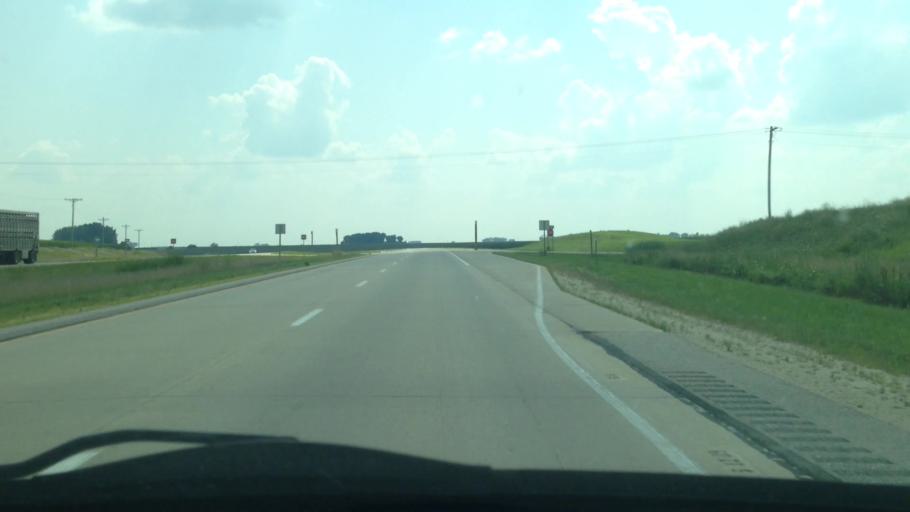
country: US
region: Iowa
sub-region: Bremer County
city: Tripoli
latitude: 42.8891
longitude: -92.3342
